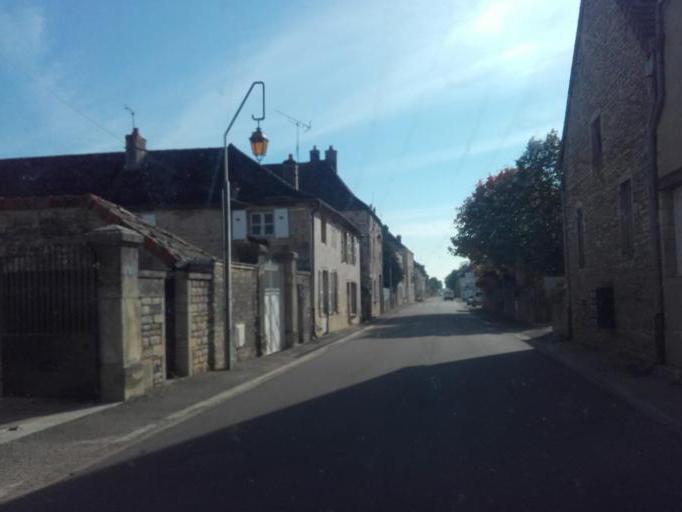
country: FR
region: Bourgogne
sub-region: Departement de Saone-et-Loire
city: Mellecey
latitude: 46.8311
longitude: 4.7262
